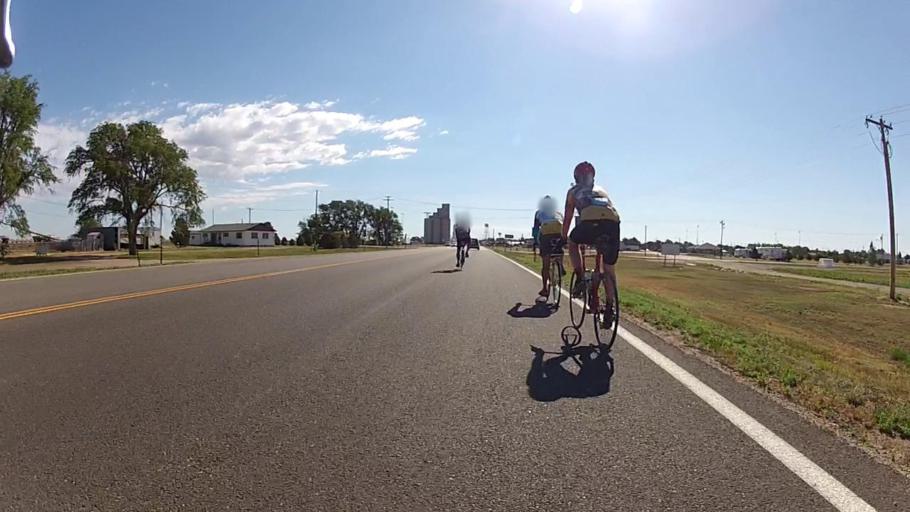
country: US
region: Kansas
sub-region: Gray County
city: Cimarron
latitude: 37.5969
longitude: -100.4529
